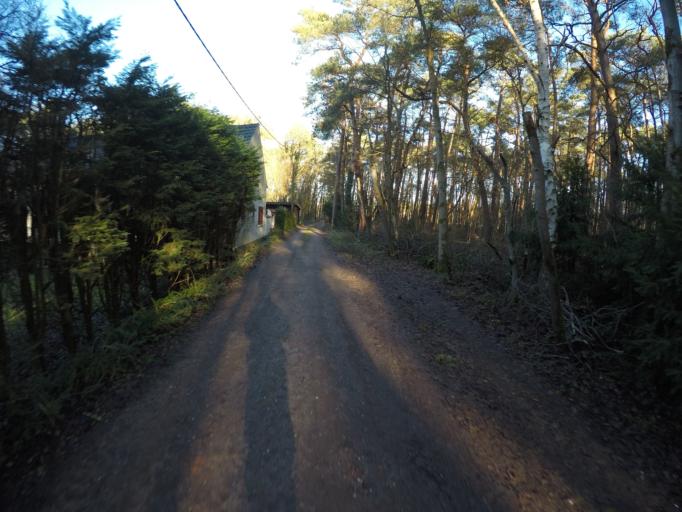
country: BE
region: Flanders
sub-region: Provincie Antwerpen
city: Schilde
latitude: 51.2389
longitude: 4.6255
